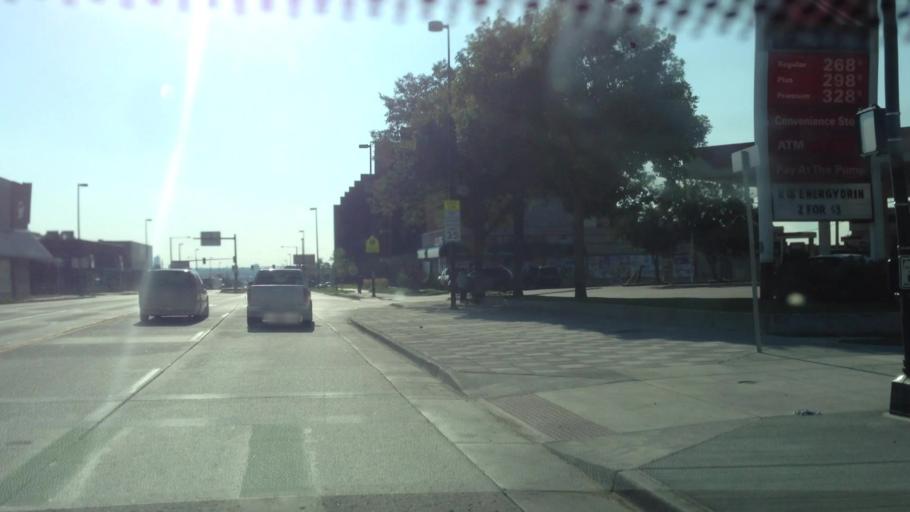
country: US
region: Colorado
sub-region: Jefferson County
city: Lakewood
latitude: 39.7112
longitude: -105.0327
